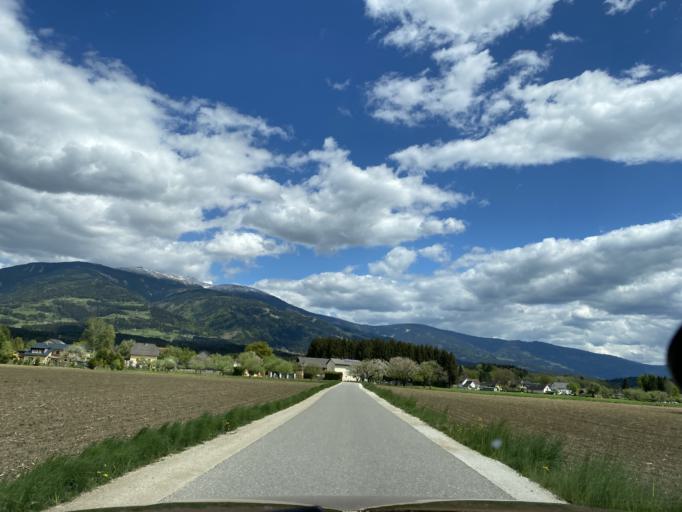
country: AT
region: Carinthia
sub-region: Politischer Bezirk Wolfsberg
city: Sankt Andrae
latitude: 46.7836
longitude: 14.8366
